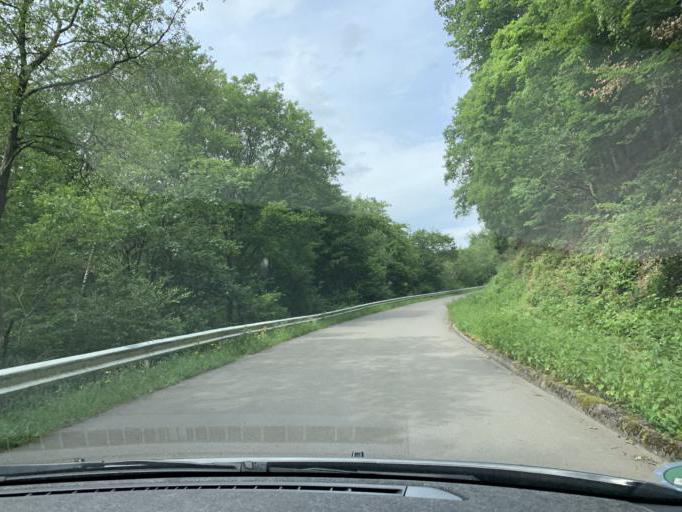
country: DE
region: North Rhine-Westphalia
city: Heimbach
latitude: 50.6512
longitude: 6.4090
